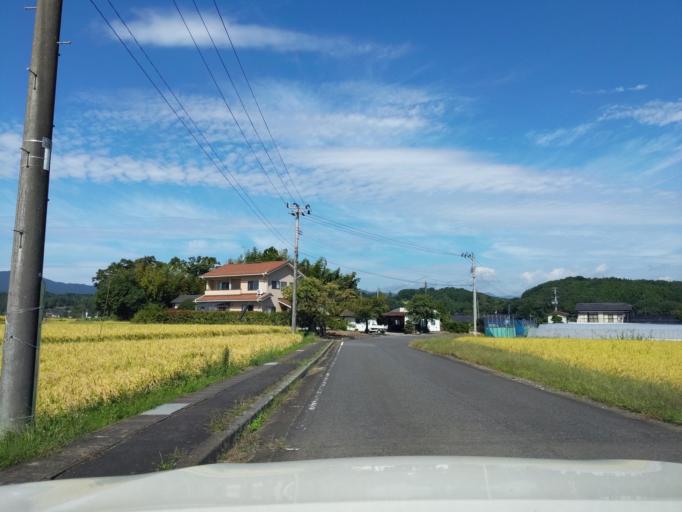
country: JP
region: Fukushima
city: Koriyama
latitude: 37.3681
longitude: 140.2868
